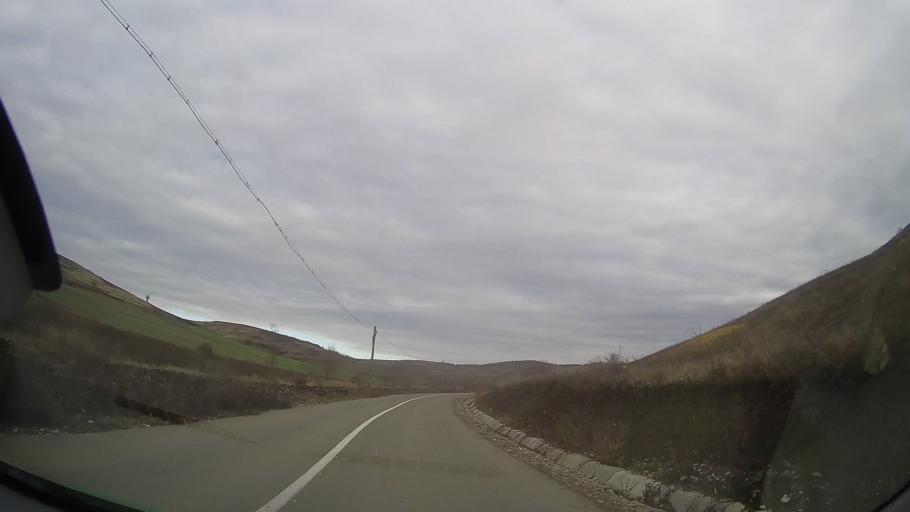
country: RO
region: Bistrita-Nasaud
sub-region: Comuna Silvasu de Campie
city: Silvasu de Campie
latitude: 46.8187
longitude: 24.2967
